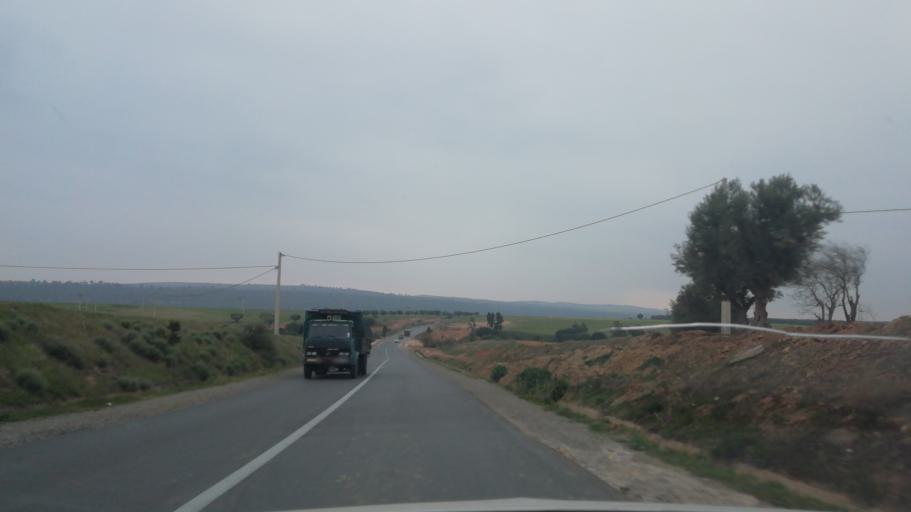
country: DZ
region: Sidi Bel Abbes
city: Sfizef
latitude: 35.2758
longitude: -0.1550
